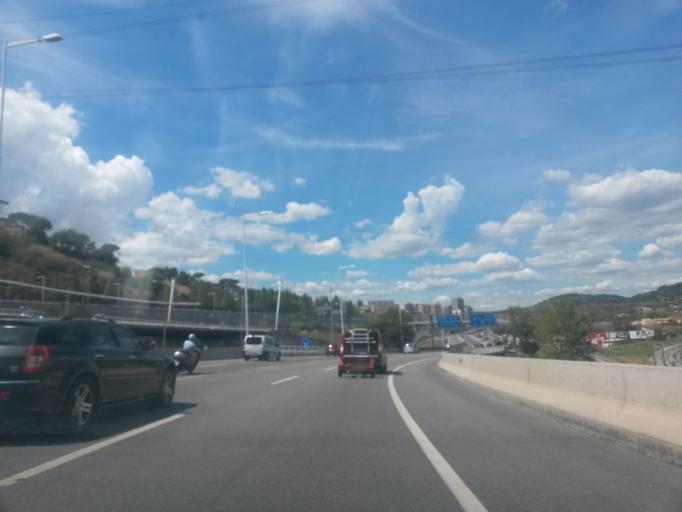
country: ES
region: Catalonia
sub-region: Provincia de Barcelona
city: Nou Barris
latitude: 41.4559
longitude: 2.1895
